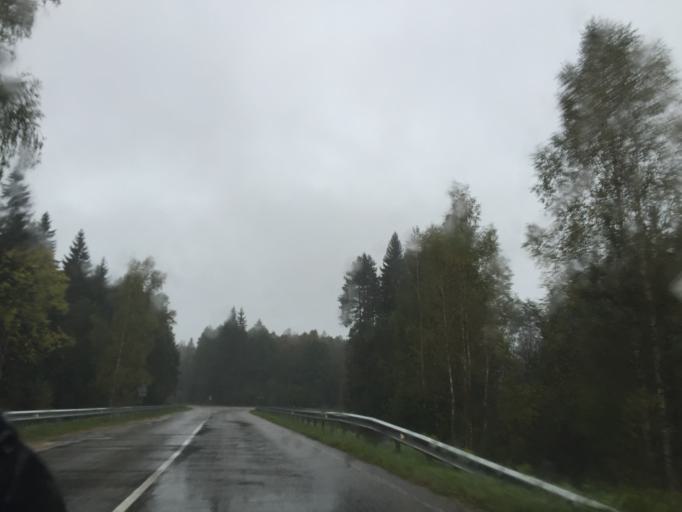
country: LV
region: Ropazu
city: Ropazi
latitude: 57.0118
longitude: 24.6810
